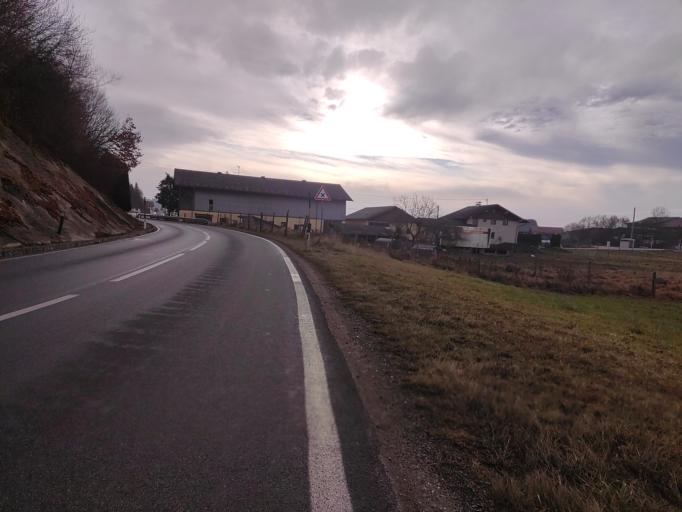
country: AT
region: Salzburg
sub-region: Politischer Bezirk Salzburg-Umgebung
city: Strasswalchen
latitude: 47.9919
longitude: 13.2427
